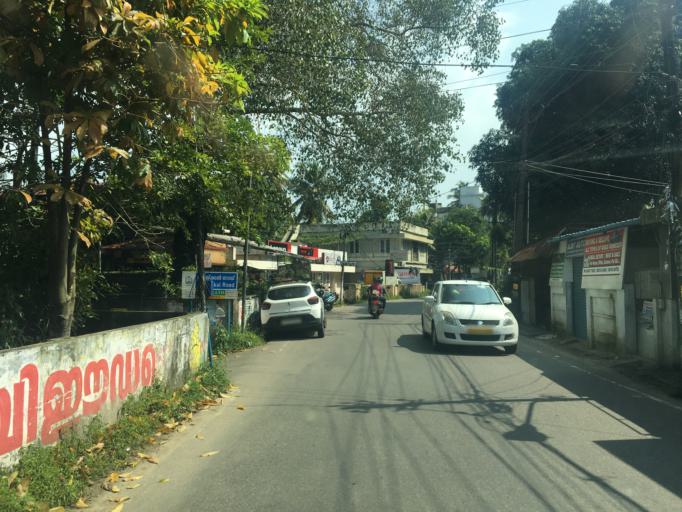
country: IN
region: Kerala
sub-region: Ernakulam
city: Cochin
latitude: 9.9623
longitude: 76.3009
